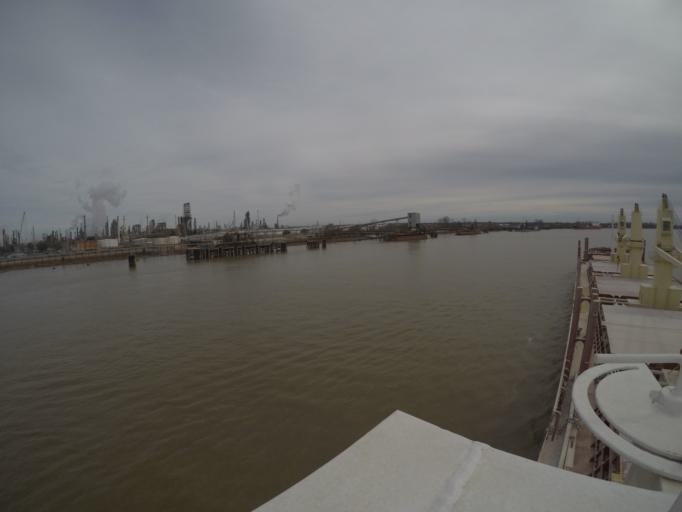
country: US
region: Louisiana
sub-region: Saint Charles Parish
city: Norco
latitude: 29.9901
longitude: -90.4070
